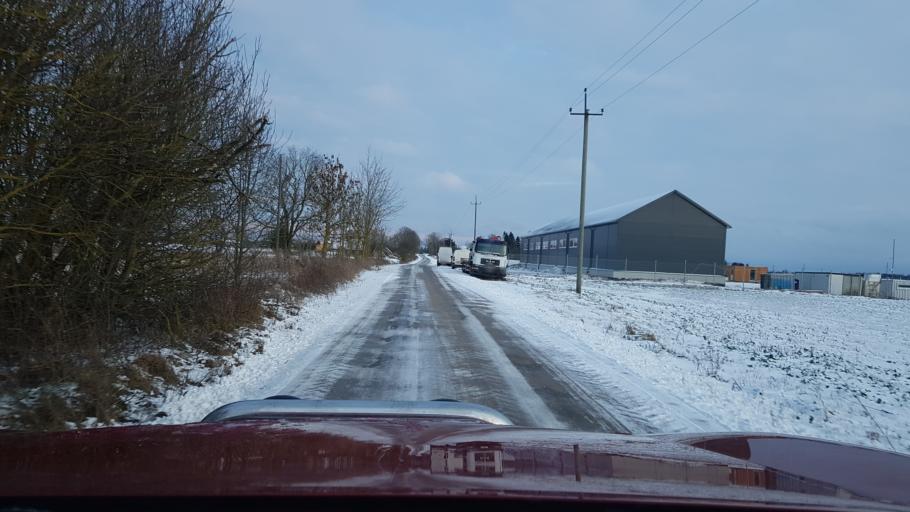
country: EE
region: Harju
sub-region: Maardu linn
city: Maardu
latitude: 59.4291
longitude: 25.0244
